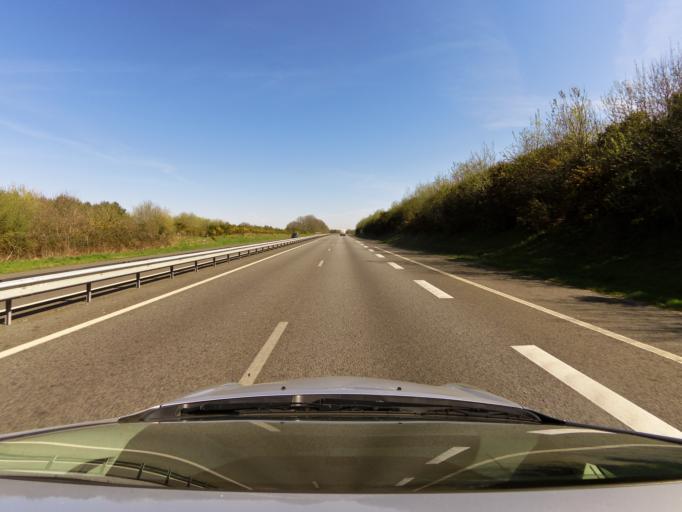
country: FR
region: Brittany
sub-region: Departement d'Ille-et-Vilaine
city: Liffre
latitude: 48.2077
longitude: -1.5238
